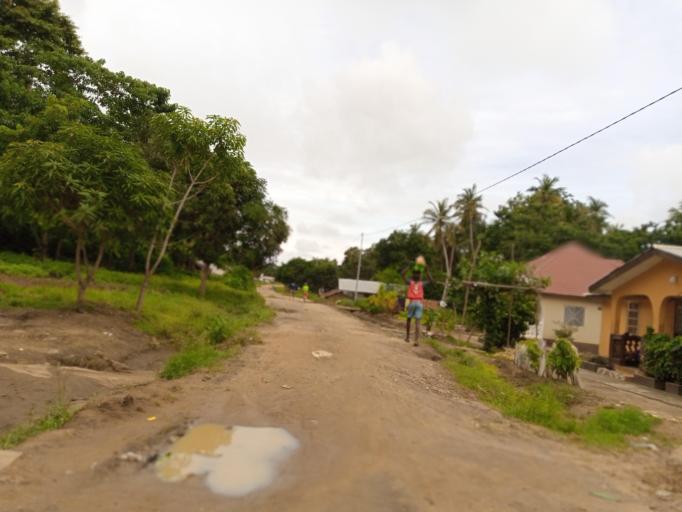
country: SL
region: Northern Province
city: Masoyila
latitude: 8.5960
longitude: -13.1978
